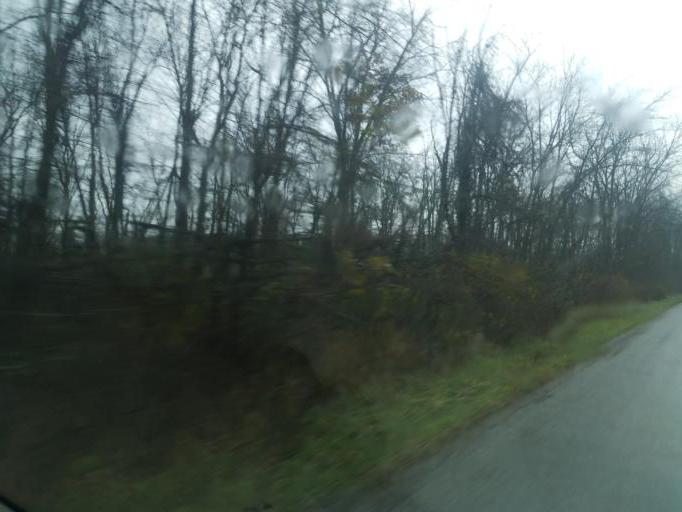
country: US
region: Ohio
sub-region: Morrow County
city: Cardington
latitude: 40.4619
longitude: -82.8857
